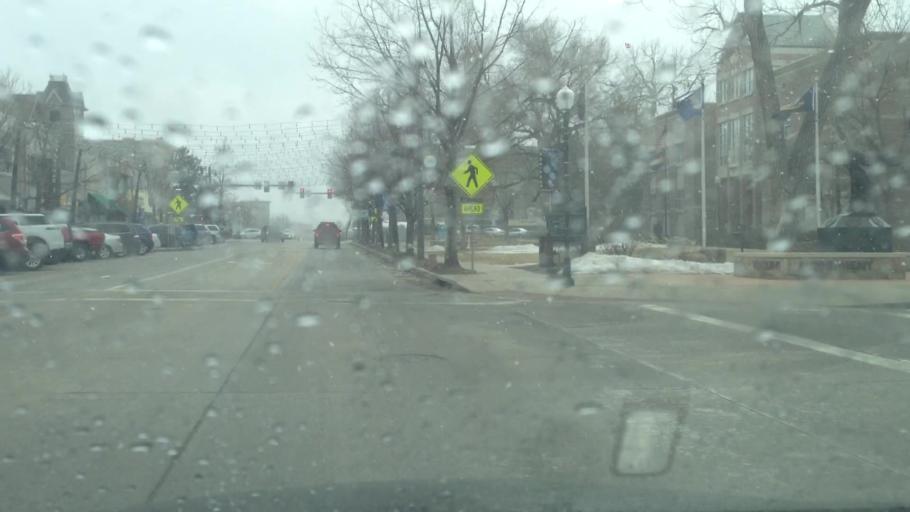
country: US
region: Colorado
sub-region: Douglas County
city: Castle Rock
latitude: 39.3734
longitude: -104.8601
